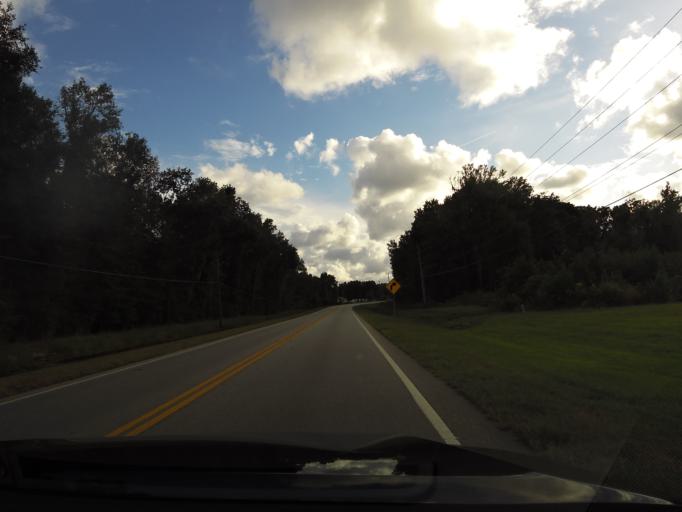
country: US
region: Georgia
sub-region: Liberty County
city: Midway
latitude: 31.7828
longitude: -81.4390
